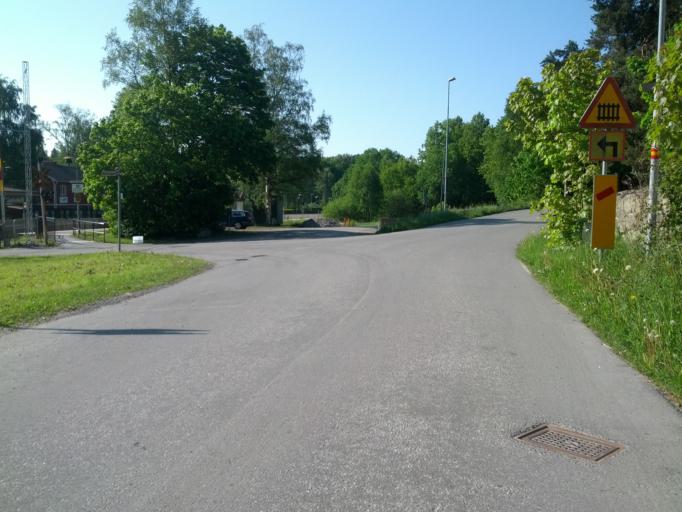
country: SE
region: Stockholm
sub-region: Taby Kommun
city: Taby
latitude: 59.4263
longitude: 18.0507
